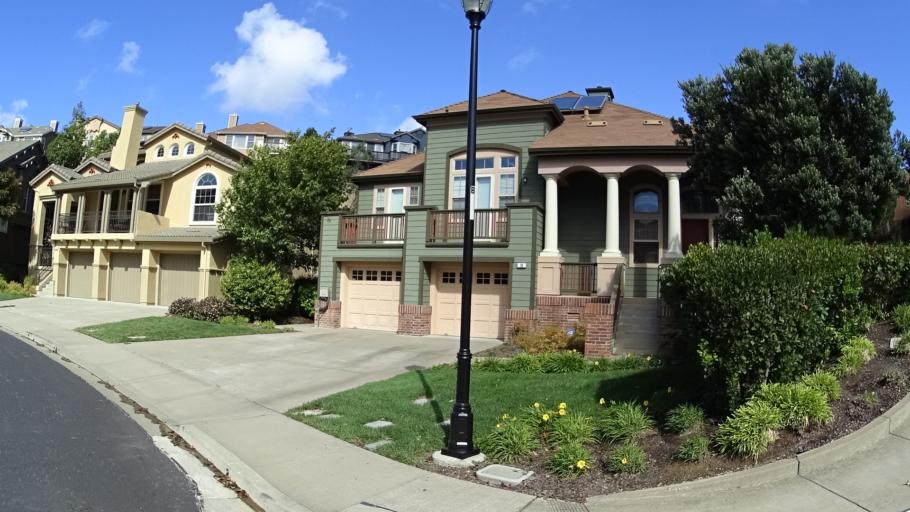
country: US
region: California
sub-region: San Mateo County
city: Brisbane
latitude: 37.6954
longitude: -122.4194
